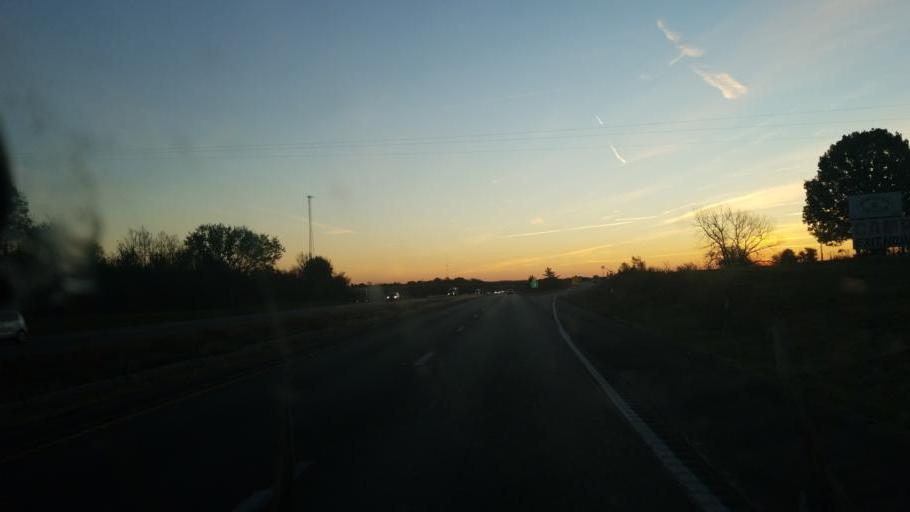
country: US
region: Missouri
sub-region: Cooper County
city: Boonville
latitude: 38.9394
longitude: -92.6023
